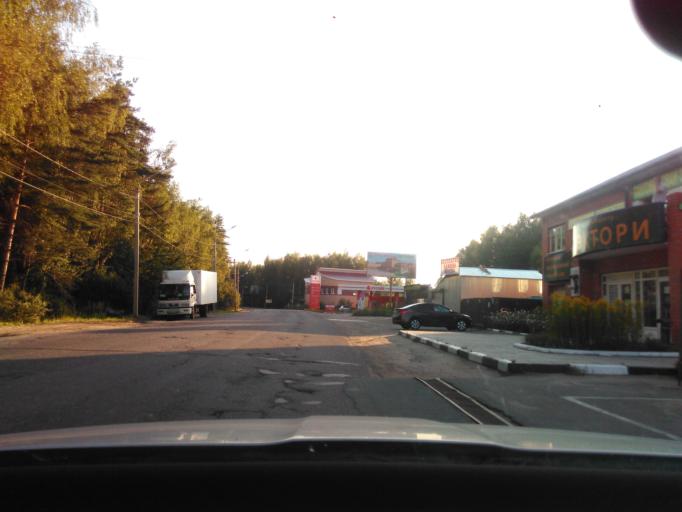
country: RU
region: Tverskaya
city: Konakovo
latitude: 56.6783
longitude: 36.7494
